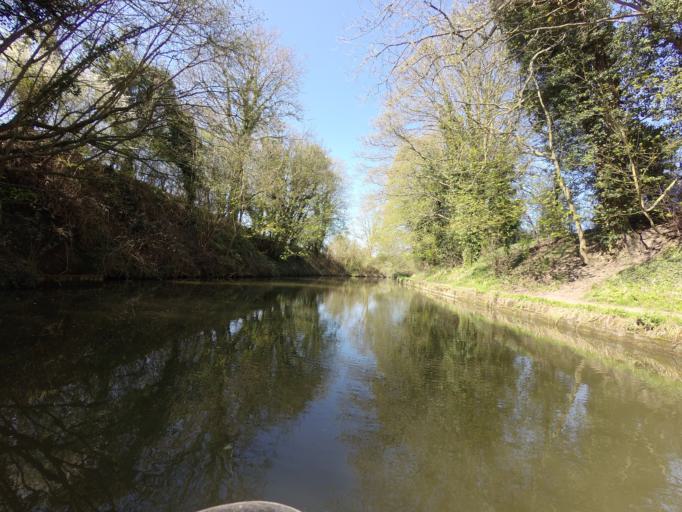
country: GB
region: England
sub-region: Hertfordshire
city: Tring
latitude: 51.7932
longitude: -0.6212
